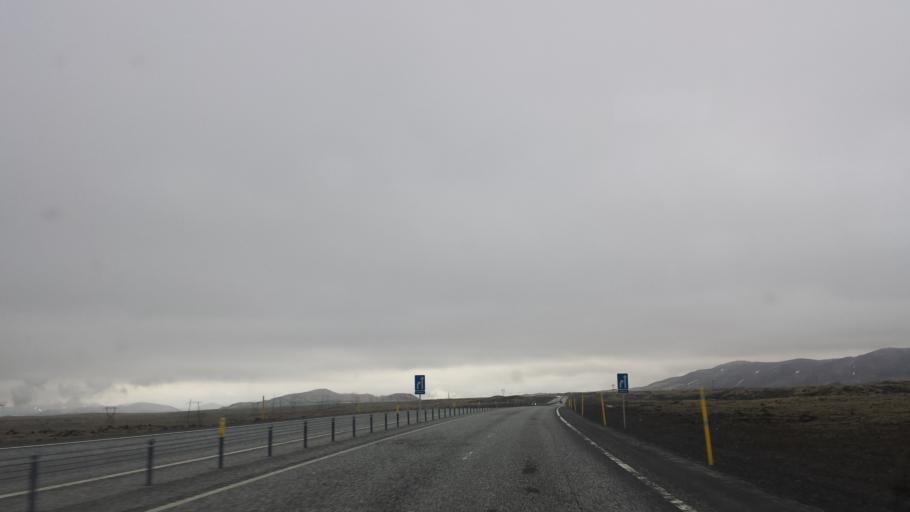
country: IS
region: South
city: Hveragerdi
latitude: 64.0151
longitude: -21.2687
